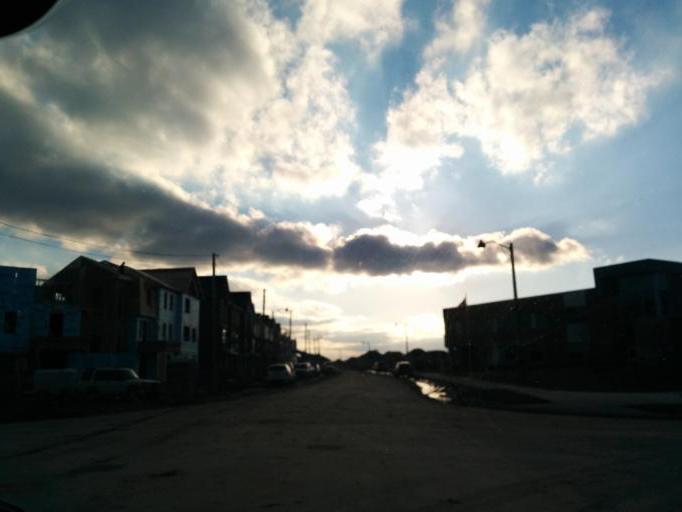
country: CA
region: Ontario
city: Oakville
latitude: 43.4721
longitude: -79.7426
